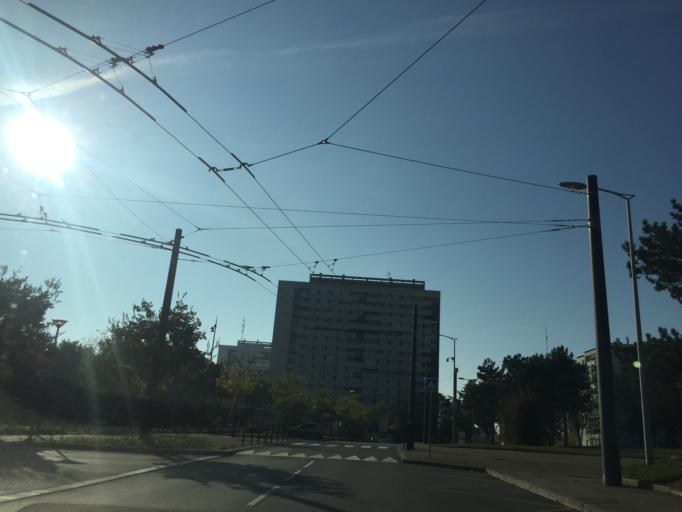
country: FR
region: Rhone-Alpes
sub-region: Departement du Rhone
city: Rillieux-la-Pape
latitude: 45.8197
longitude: 4.9097
